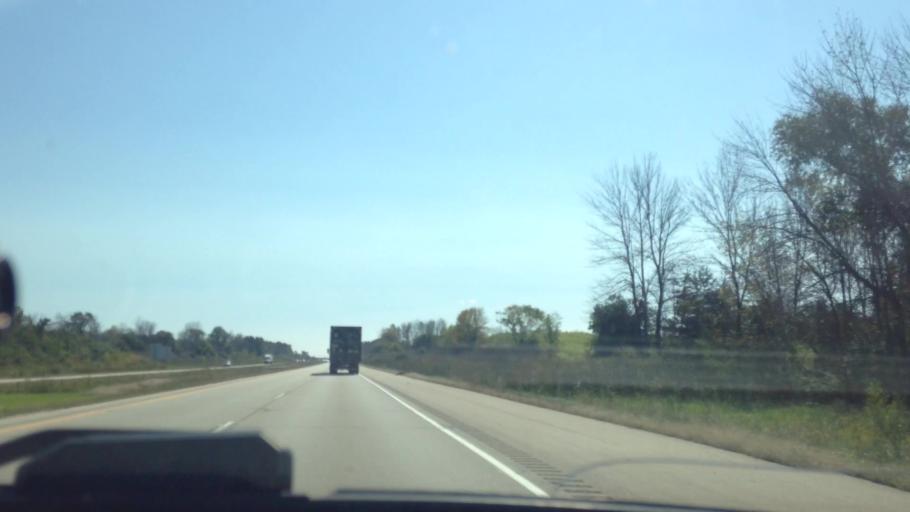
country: US
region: Wisconsin
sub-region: Ozaukee County
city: Thiensville
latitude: 43.2640
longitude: -87.9201
